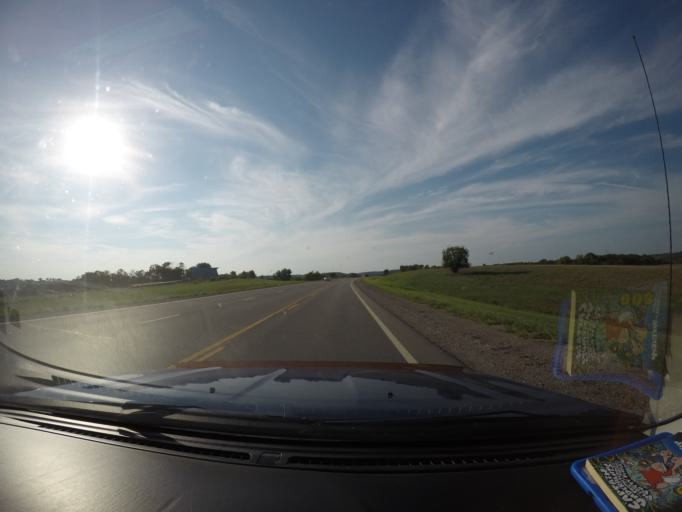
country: US
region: Kansas
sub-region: Atchison County
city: Atchison
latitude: 39.4731
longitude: -95.1004
